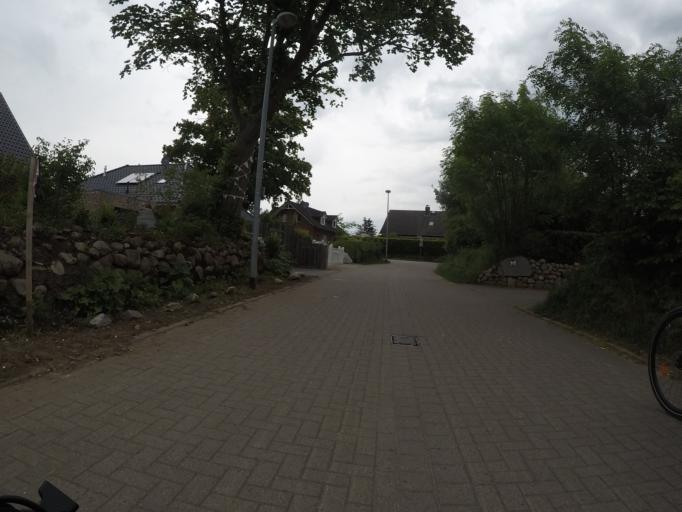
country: DE
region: Schleswig-Holstein
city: Kisdorf
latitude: 53.7859
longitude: 10.0129
